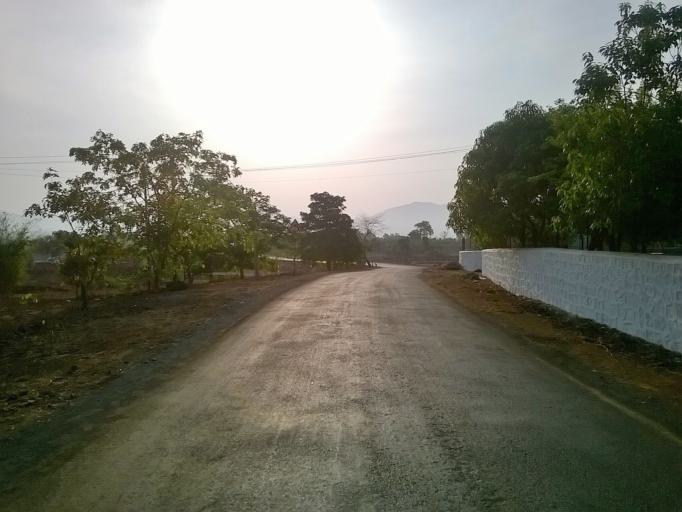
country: IN
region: Maharashtra
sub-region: Raigarh
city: Matheran
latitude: 19.0289
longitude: 73.2140
